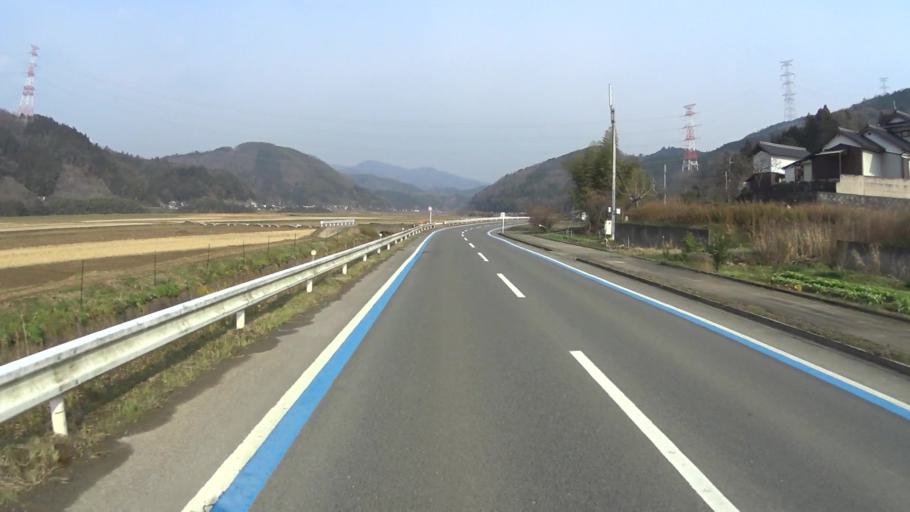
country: JP
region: Kyoto
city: Fukuchiyama
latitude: 35.3481
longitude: 135.1148
